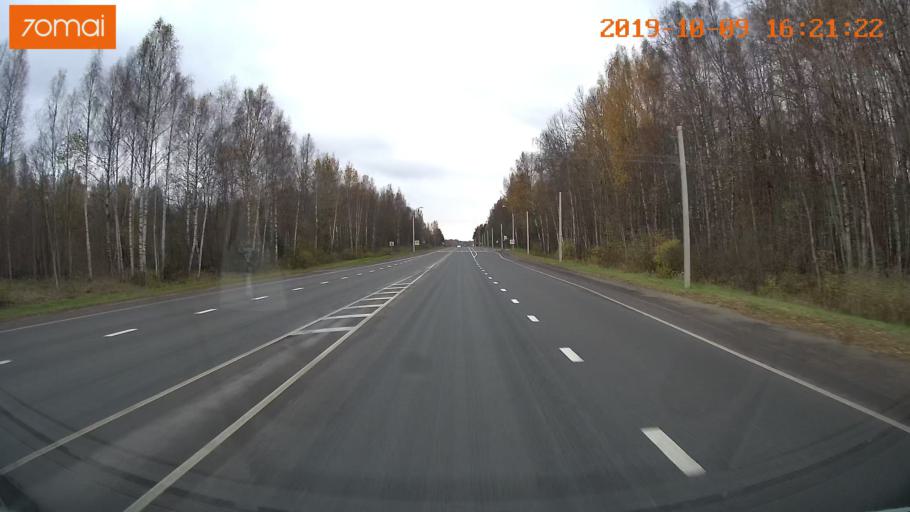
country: RU
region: Kostroma
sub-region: Kostromskoy Rayon
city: Kostroma
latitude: 57.6931
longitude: 40.8894
